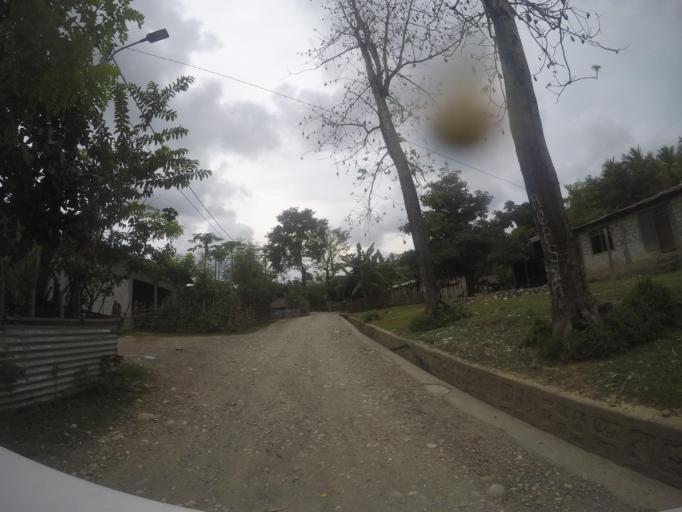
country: TL
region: Viqueque
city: Viqueque
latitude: -8.8773
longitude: 126.3639
